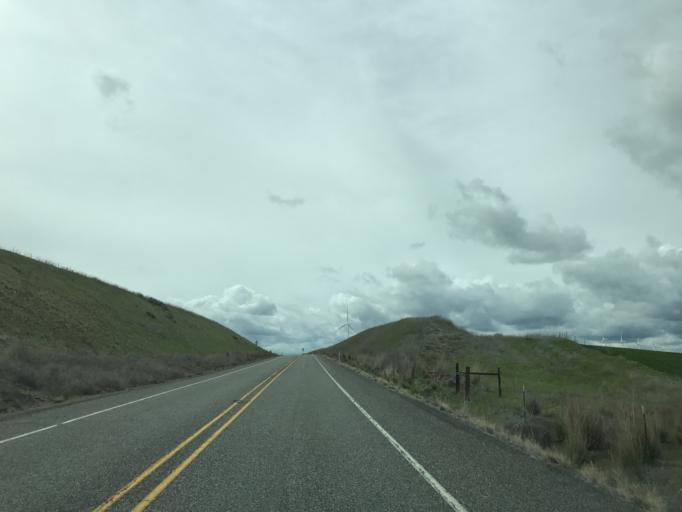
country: US
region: Washington
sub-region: Garfield County
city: Pomeroy
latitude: 46.5255
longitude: -117.7896
